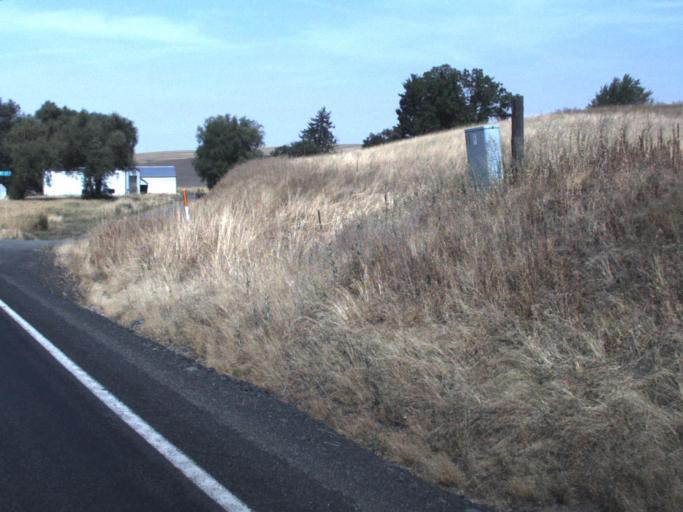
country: US
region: Washington
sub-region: Whitman County
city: Colfax
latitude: 47.0968
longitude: -117.1697
